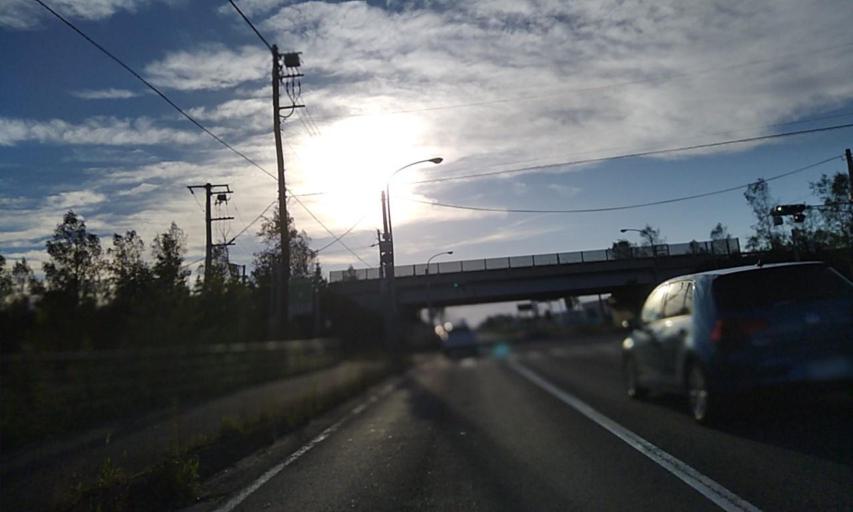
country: JP
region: Hokkaido
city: Obihiro
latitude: 42.9251
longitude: 143.1100
